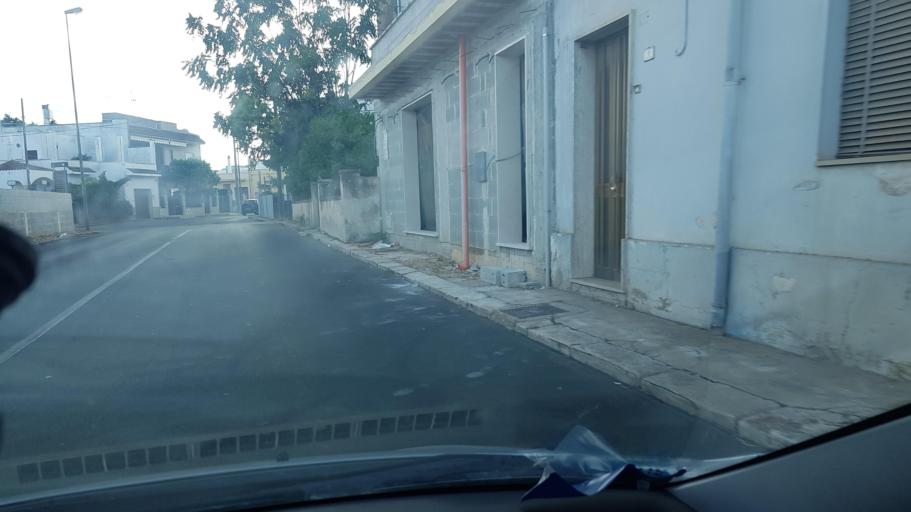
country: IT
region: Apulia
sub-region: Provincia di Brindisi
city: Cellino San Marco
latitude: 40.4703
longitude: 17.9697
